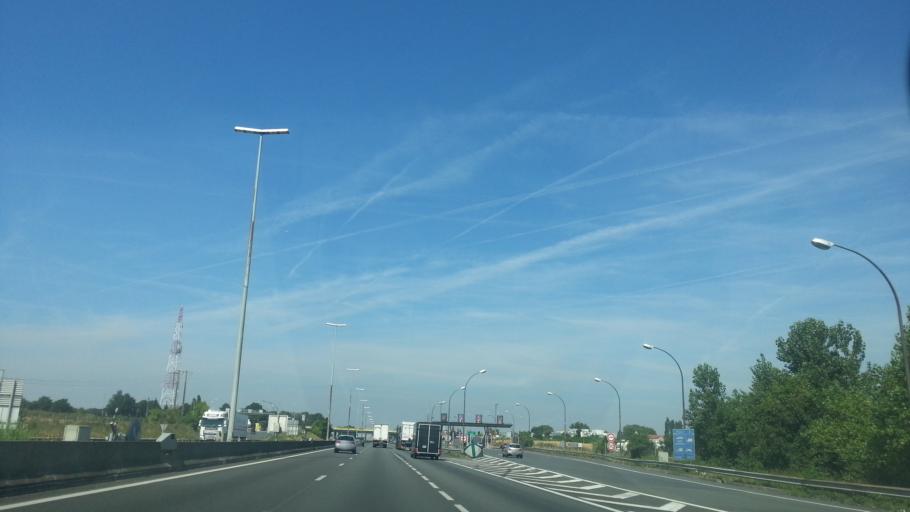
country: FR
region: Ile-de-France
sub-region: Departement du Val-d'Oise
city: Survilliers
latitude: 49.0825
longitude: 2.5514
